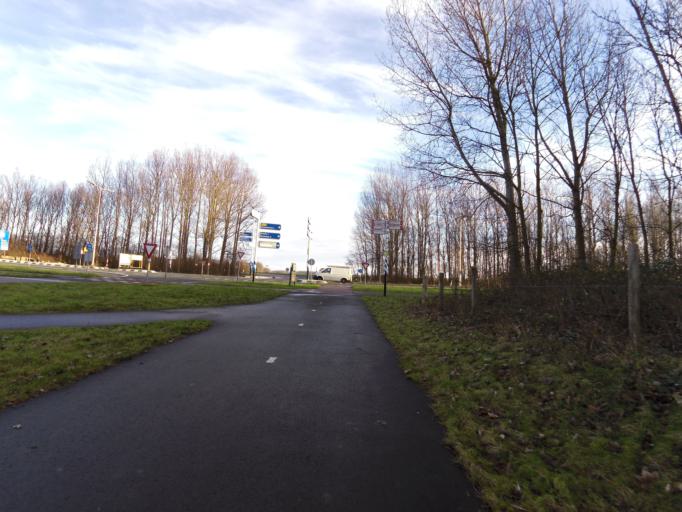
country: NL
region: South Holland
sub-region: Gemeente Rotterdam
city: Hoek van Holland
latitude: 51.9311
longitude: 4.1026
